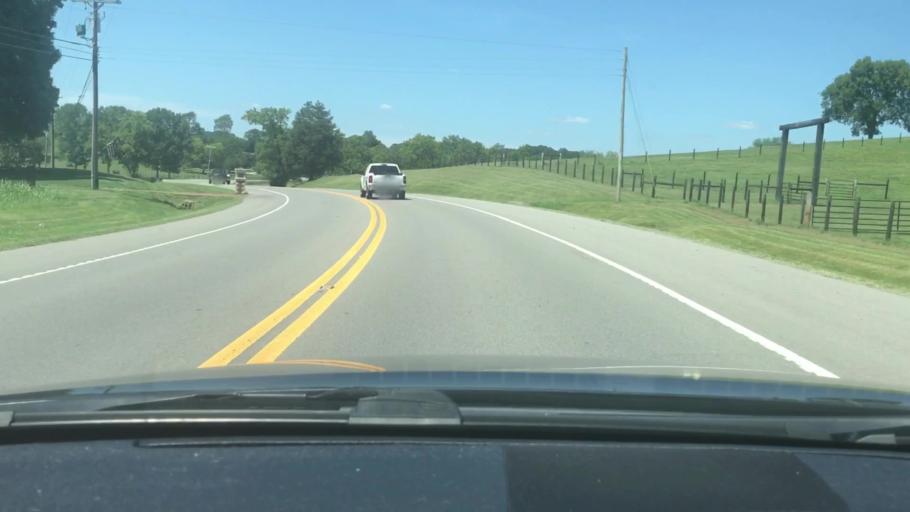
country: US
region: Tennessee
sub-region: Sumner County
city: Shackle Island
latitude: 36.4528
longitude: -86.5397
